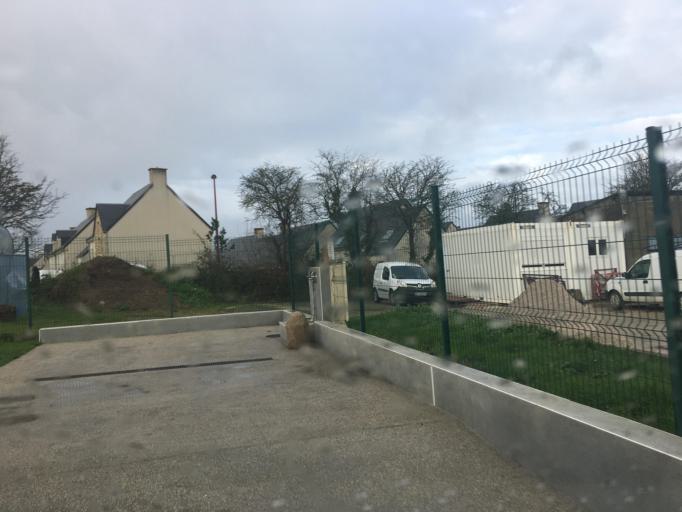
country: FR
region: Lower Normandy
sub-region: Departement de la Manche
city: Saint-Pierre-Eglise
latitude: 49.6719
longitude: -1.4045
